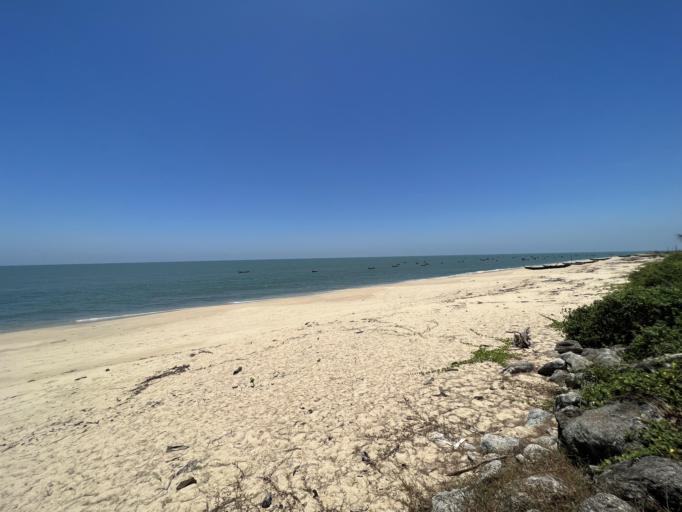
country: MM
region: Tanintharyi
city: Dawei
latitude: 14.5730
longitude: 97.9064
